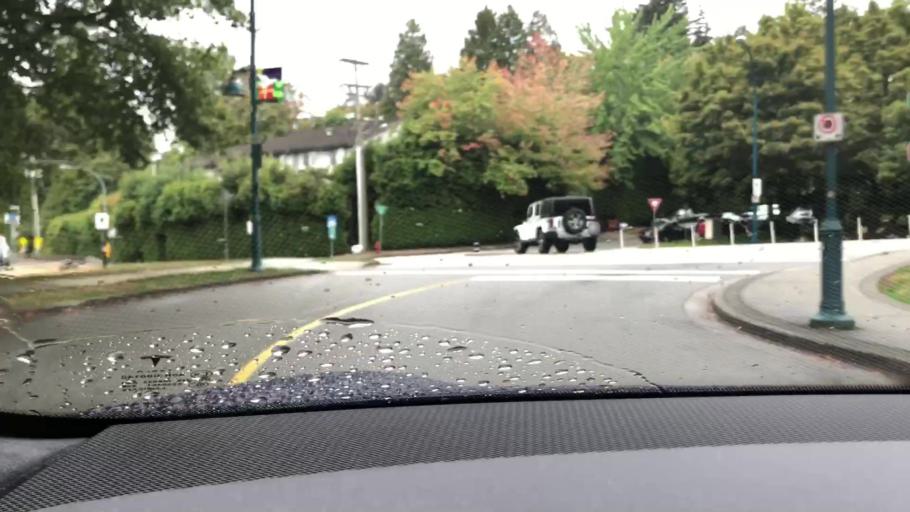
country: CA
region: British Columbia
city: Port Moody
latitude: 49.2837
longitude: -122.8299
